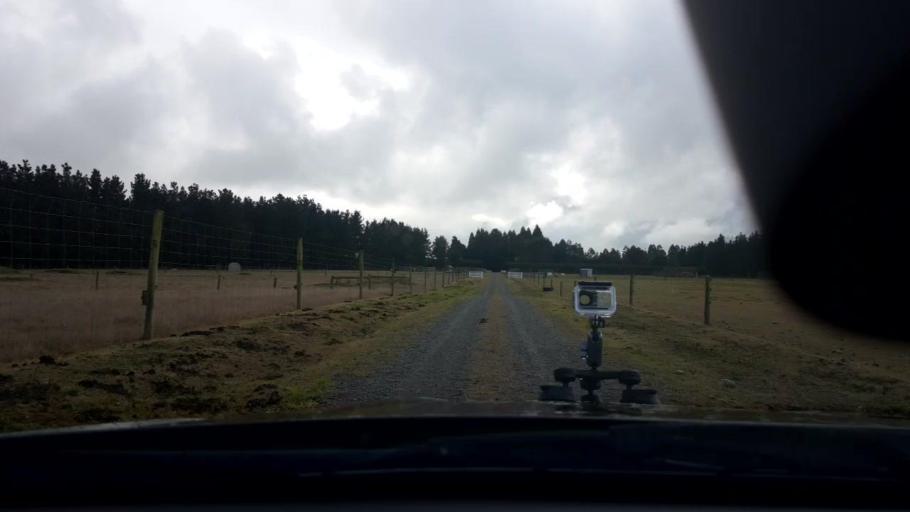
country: NZ
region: Canterbury
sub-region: Waimakariri District
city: Oxford
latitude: -43.4019
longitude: 172.3117
